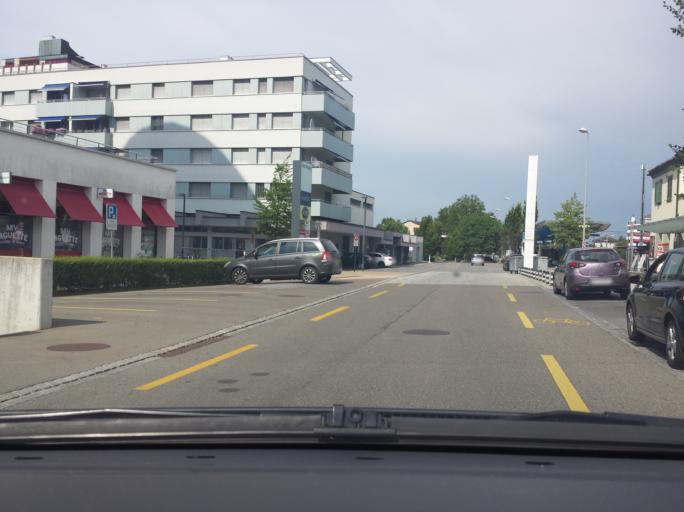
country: CH
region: Appenzell Innerrhoden
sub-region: Appenzell Inner Rhodes
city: Balgach
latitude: 47.4103
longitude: 9.6266
